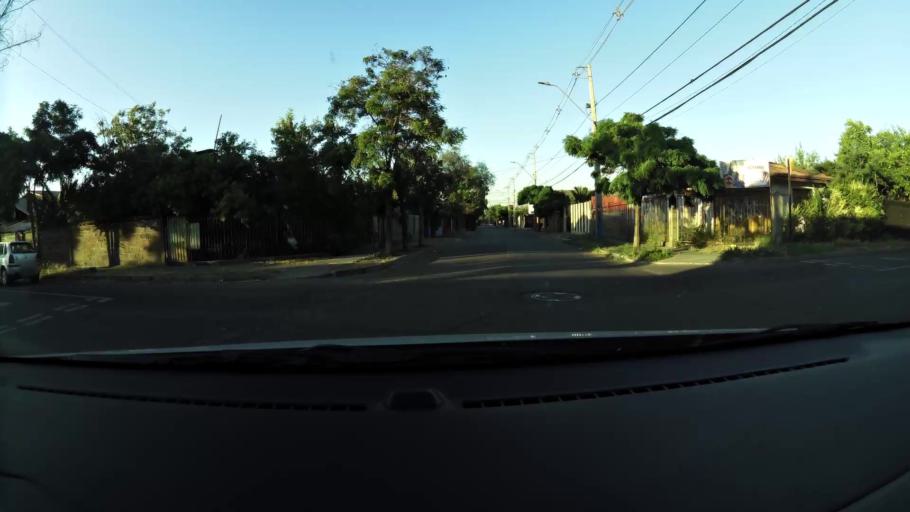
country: CL
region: Santiago Metropolitan
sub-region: Provincia de Maipo
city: San Bernardo
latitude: -33.5831
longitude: -70.7034
